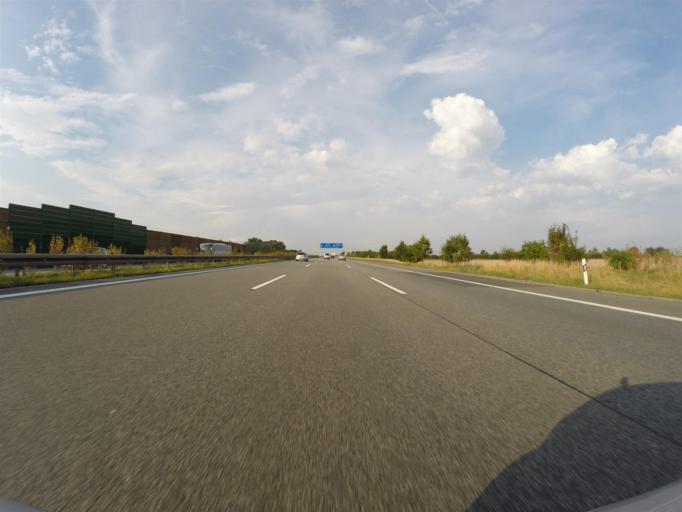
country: DE
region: Thuringia
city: Walpernhain
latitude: 51.0316
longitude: 11.9381
